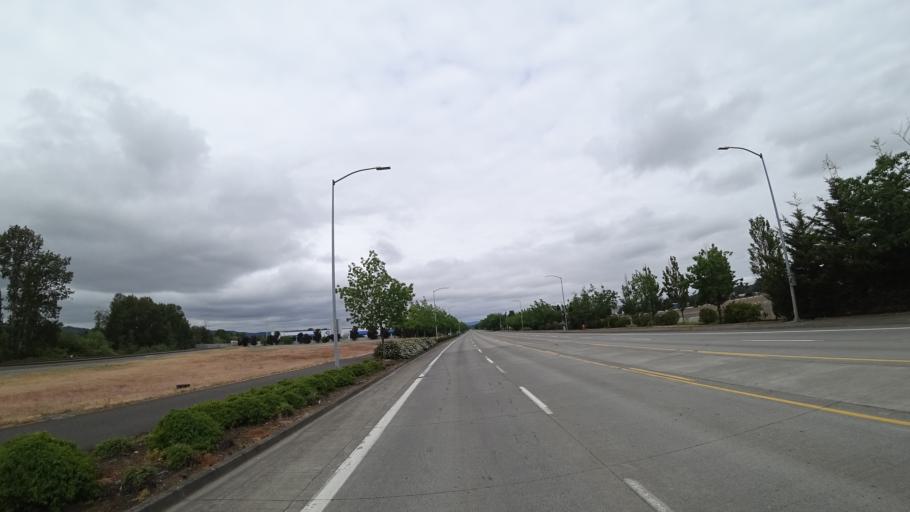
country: US
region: Washington
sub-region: Clark County
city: Vancouver
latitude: 45.6235
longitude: -122.7331
